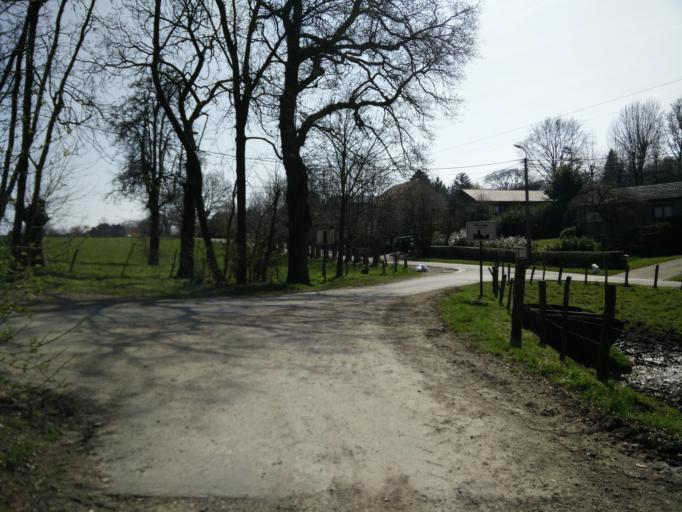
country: BE
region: Flanders
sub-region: Provincie Limburg
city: Sint-Pieters-Voeren
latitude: 50.7400
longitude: 5.7907
